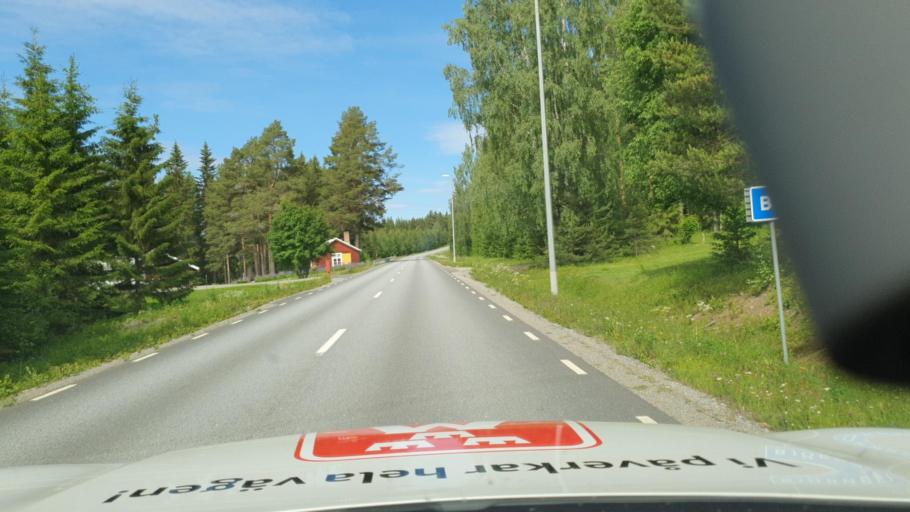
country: SE
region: Vaesterbotten
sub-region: Skelleftea Kommun
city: Forsbacka
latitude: 64.7085
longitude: 20.4319
